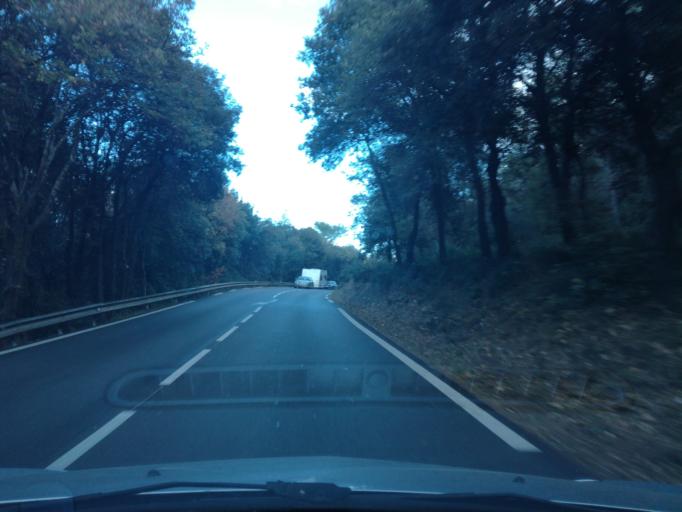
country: FR
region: Provence-Alpes-Cote d'Azur
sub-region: Departement des Alpes-Maritimes
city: Vallauris
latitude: 43.6037
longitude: 7.0418
